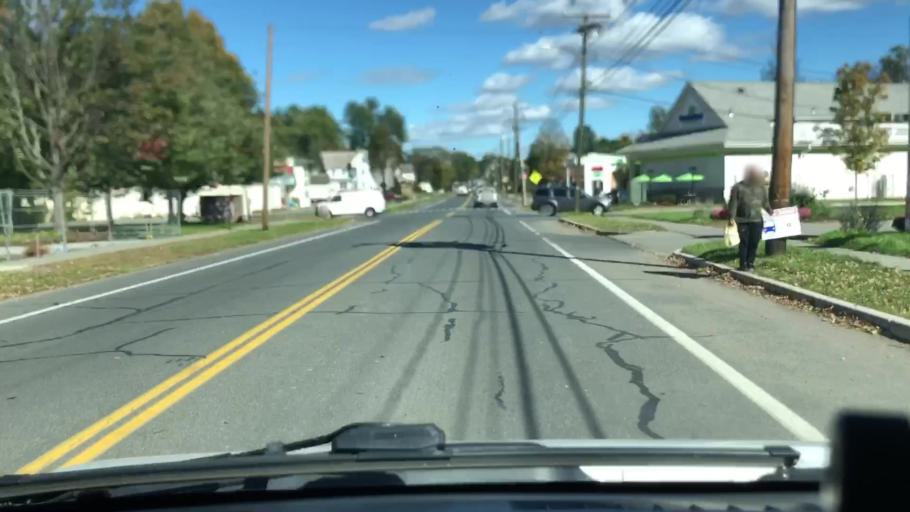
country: US
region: Massachusetts
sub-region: Franklin County
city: Greenfield
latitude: 42.6006
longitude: -72.5942
